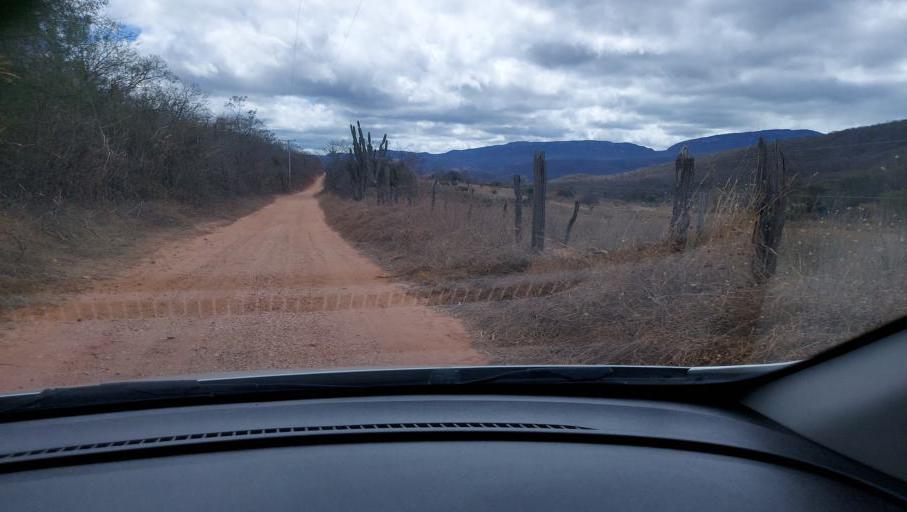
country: BR
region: Bahia
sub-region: Oliveira Dos Brejinhos
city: Beira Rio
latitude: -12.0714
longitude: -42.5389
